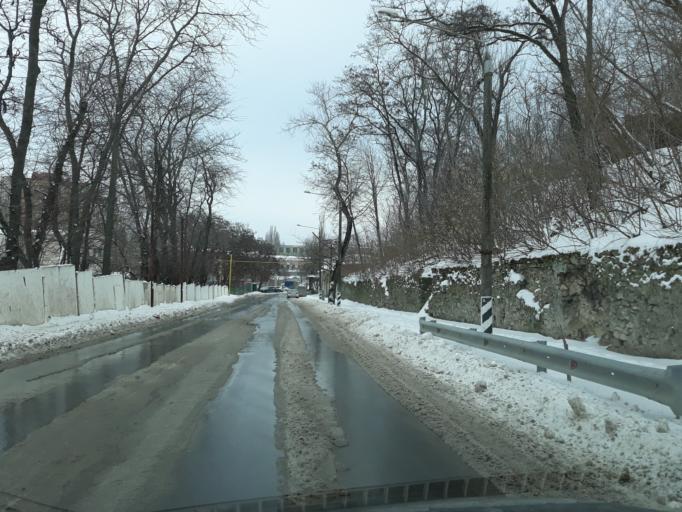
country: RU
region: Rostov
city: Taganrog
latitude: 47.2168
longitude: 38.9308
